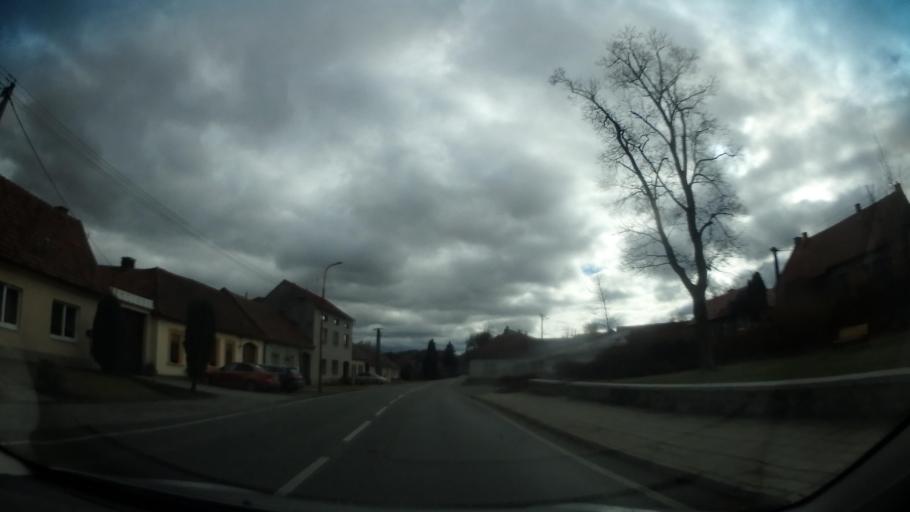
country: CZ
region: Vysocina
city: Budisov
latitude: 49.2876
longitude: 16.0961
